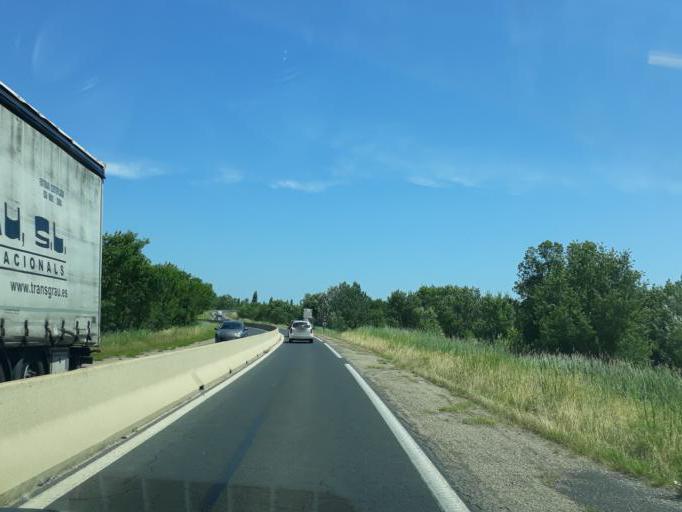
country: FR
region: Languedoc-Roussillon
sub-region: Departement de l'Herault
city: Vias
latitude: 43.3066
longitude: 3.4129
